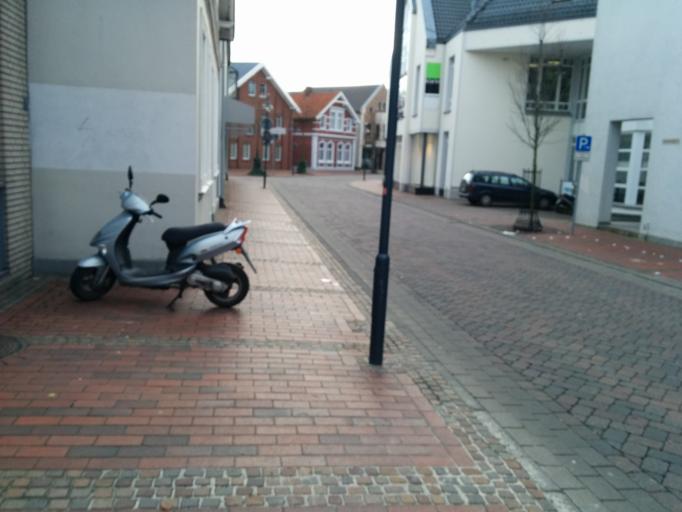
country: DE
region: Lower Saxony
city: Vechta
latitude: 52.7304
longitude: 8.2898
